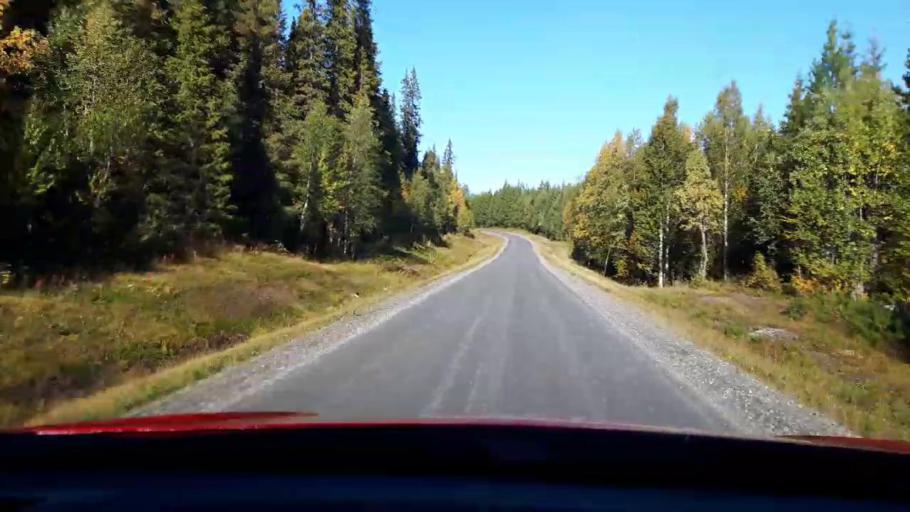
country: NO
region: Nord-Trondelag
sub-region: Lierne
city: Sandvika
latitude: 64.5319
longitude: 14.0376
